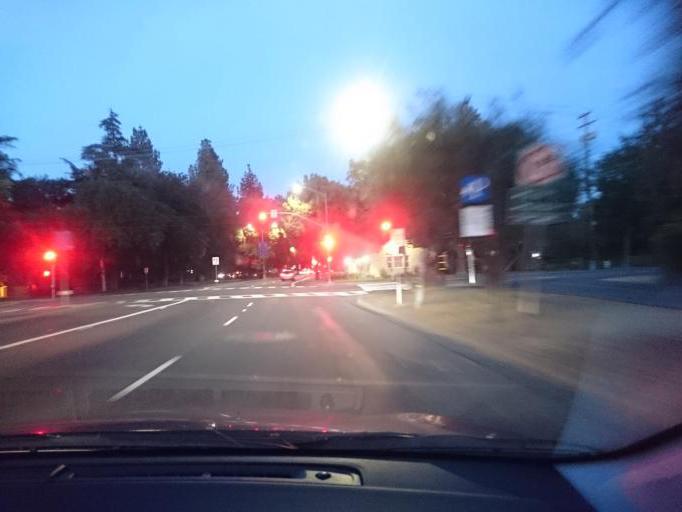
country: US
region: California
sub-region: Yolo County
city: Davis
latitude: 38.5461
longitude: -121.7482
